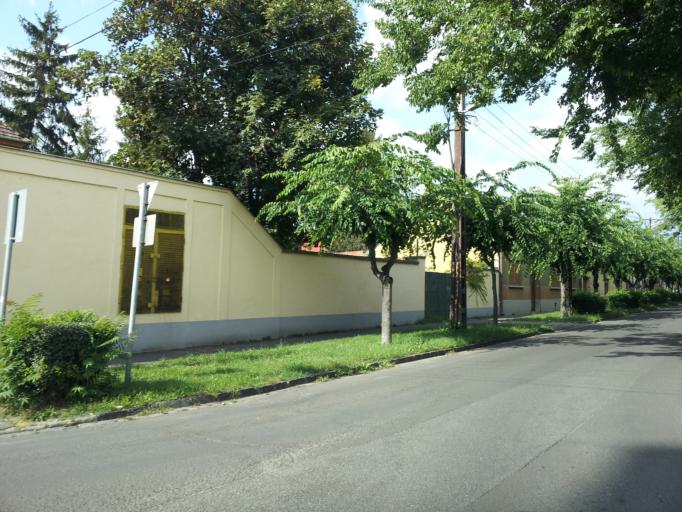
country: HU
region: Pest
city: Vac
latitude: 47.7764
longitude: 19.1321
